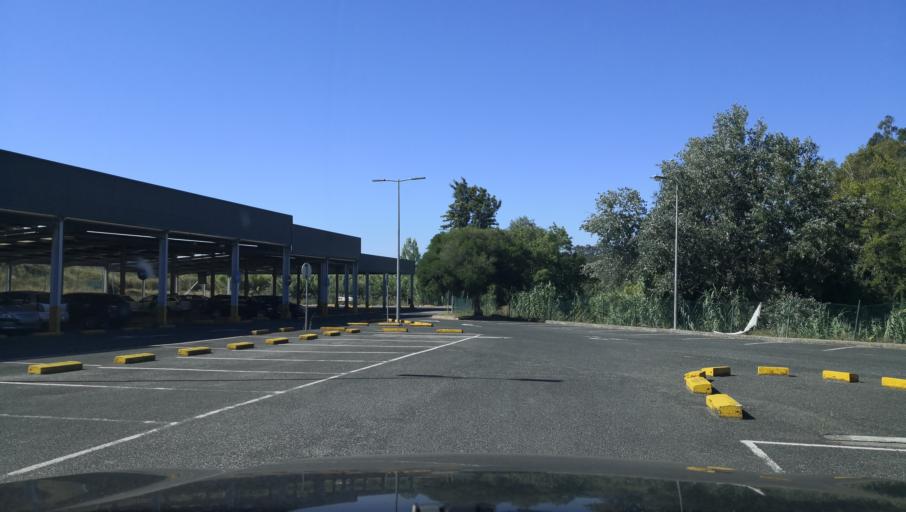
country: PT
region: Santarem
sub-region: Santarem
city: Santarem
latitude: 39.2380
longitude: -8.7042
